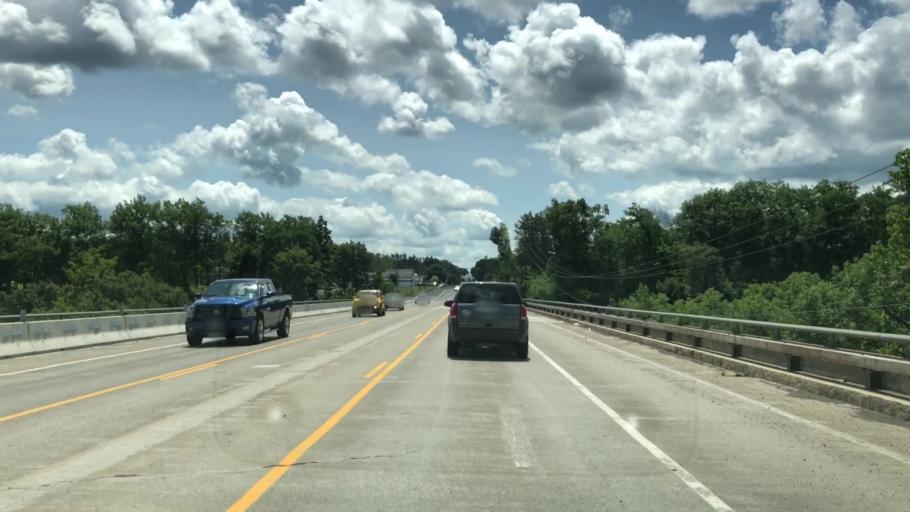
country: US
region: New York
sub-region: Erie County
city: Elma Center
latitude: 42.8167
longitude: -78.6969
